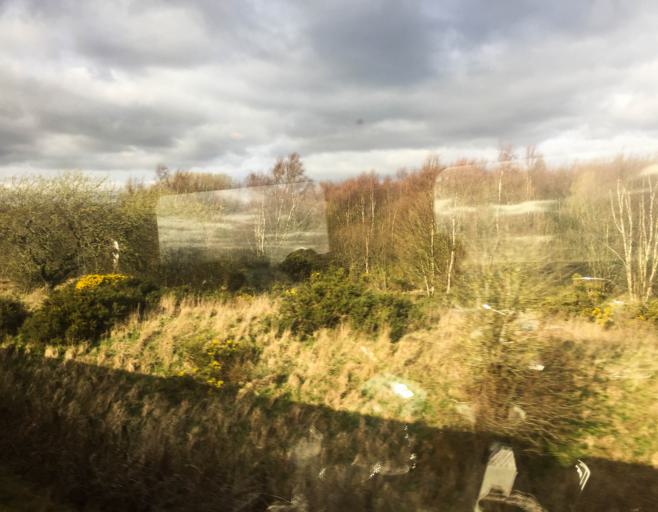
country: GB
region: Scotland
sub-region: South Lanarkshire
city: Carluke
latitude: 55.7068
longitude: -3.8226
